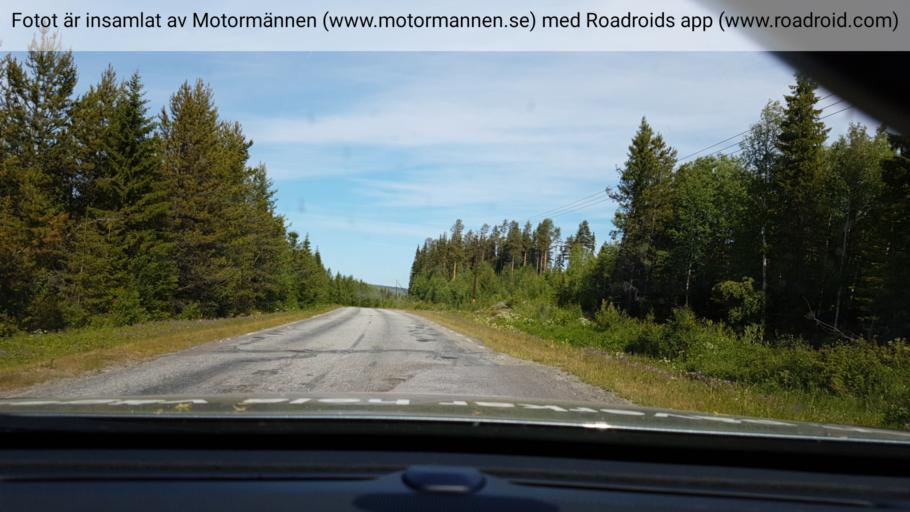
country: SE
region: Vaesterbotten
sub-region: Vilhelmina Kommun
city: Sjoberg
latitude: 64.5180
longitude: 15.9152
